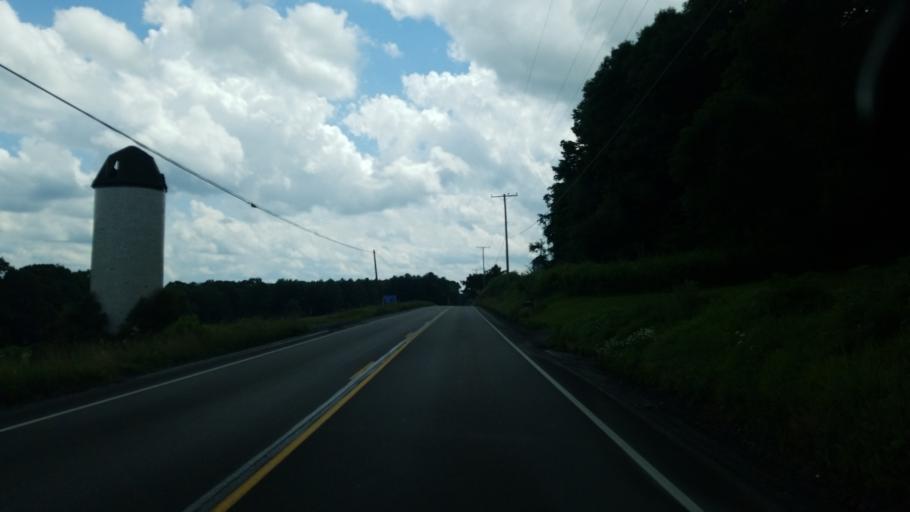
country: US
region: Pennsylvania
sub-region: Jefferson County
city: Brookville
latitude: 41.2290
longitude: -79.1119
